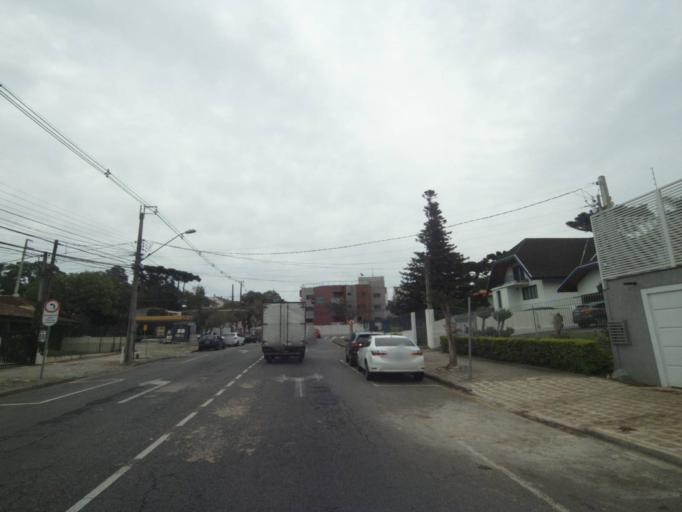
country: BR
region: Parana
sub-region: Curitiba
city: Curitiba
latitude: -25.4035
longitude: -49.2746
